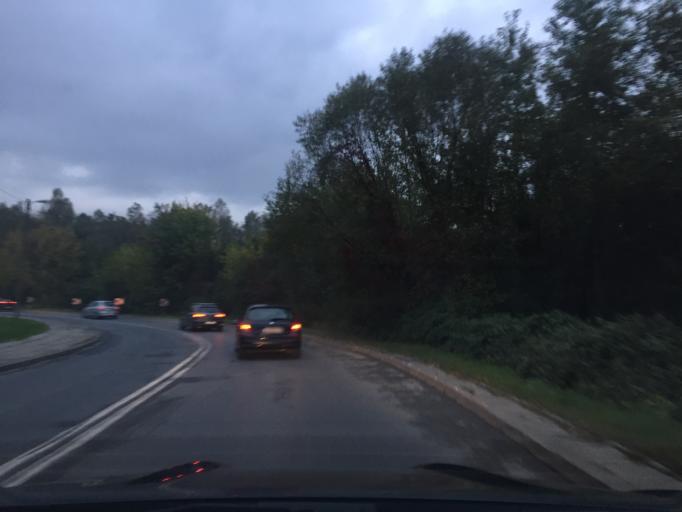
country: PL
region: Lesser Poland Voivodeship
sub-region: Powiat krakowski
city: Wrzasowice
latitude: 50.0062
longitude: 19.9371
